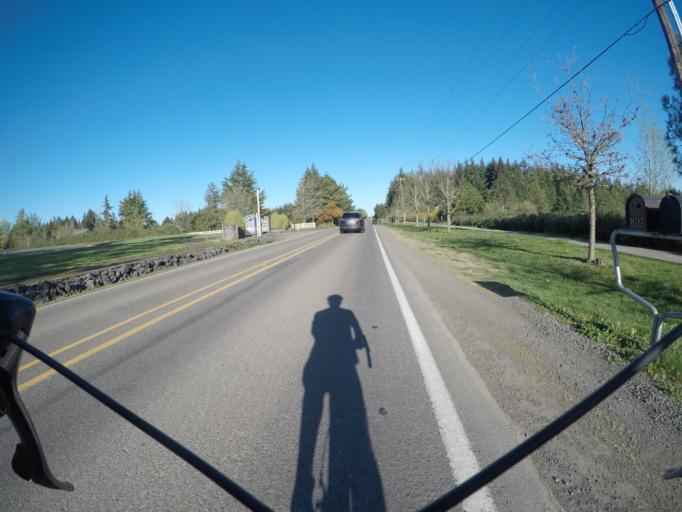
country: US
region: Oregon
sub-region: Washington County
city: Aloha
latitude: 45.4530
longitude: -122.8709
